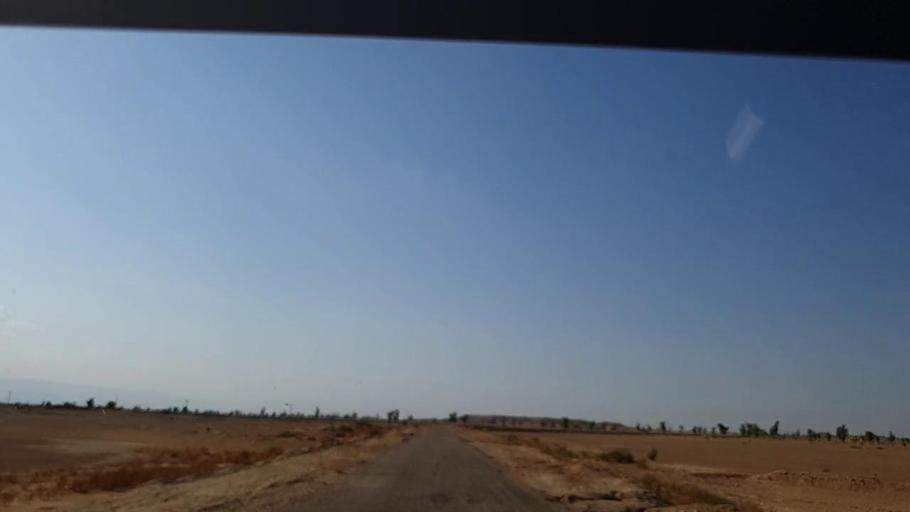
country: PK
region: Sindh
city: Johi
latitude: 26.5301
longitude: 67.5085
